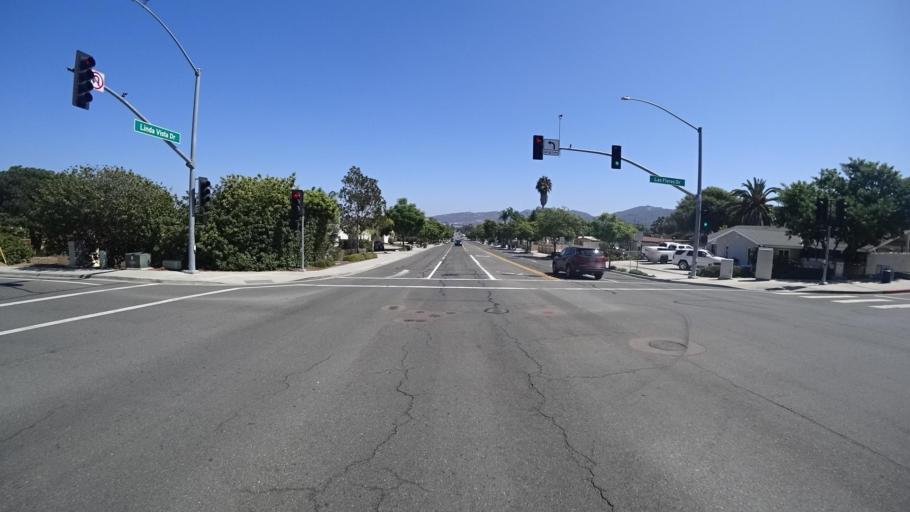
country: US
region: California
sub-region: San Diego County
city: Lake San Marcos
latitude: 33.1418
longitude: -117.2075
